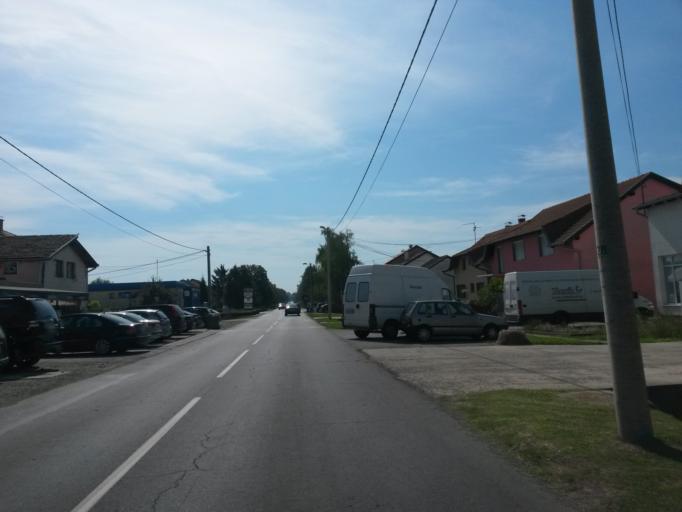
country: HR
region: Osjecko-Baranjska
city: Tenja
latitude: 45.5177
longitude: 18.7301
